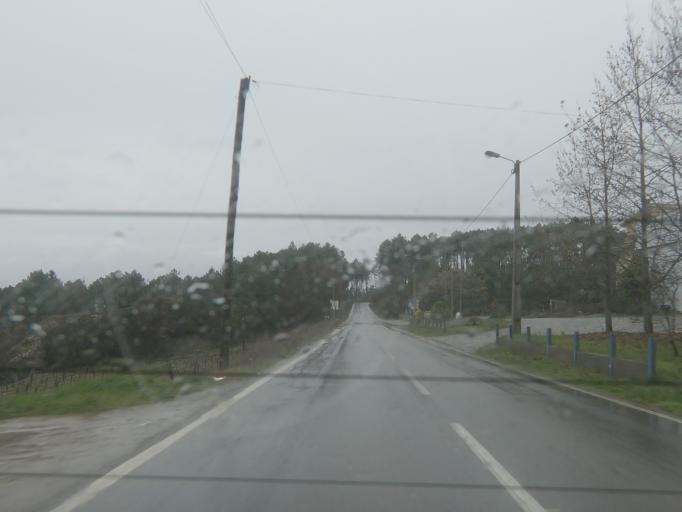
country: PT
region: Vila Real
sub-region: Sabrosa
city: Vilela
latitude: 41.2254
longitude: -7.6775
